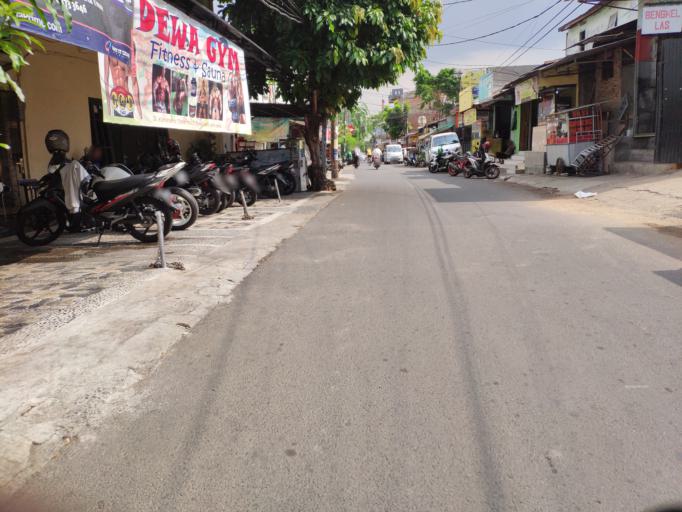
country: ID
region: Jakarta Raya
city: Jakarta
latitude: -6.1954
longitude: 106.8609
